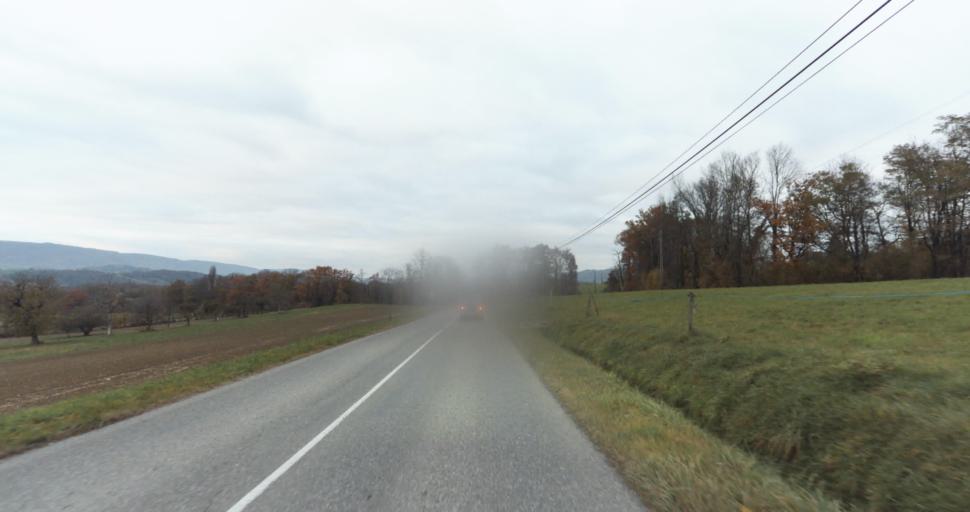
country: FR
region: Rhone-Alpes
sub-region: Departement de la Haute-Savoie
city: Saint-Felix
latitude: 45.8109
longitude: 5.9732
